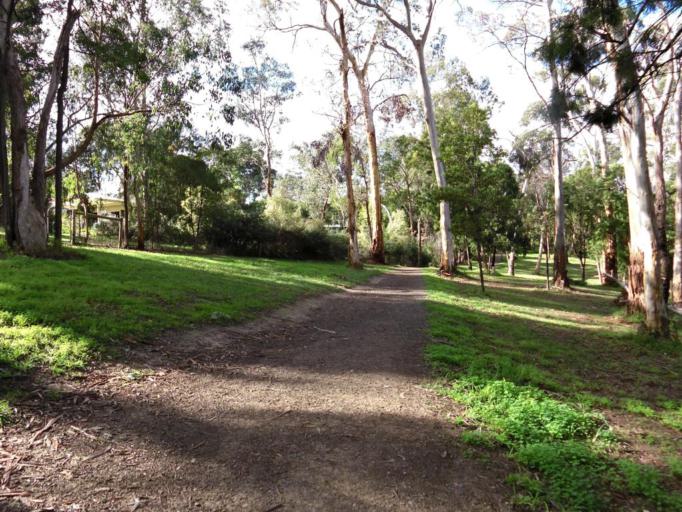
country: AU
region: Victoria
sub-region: Manningham
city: Park Orchards
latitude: -37.7727
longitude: 145.2214
